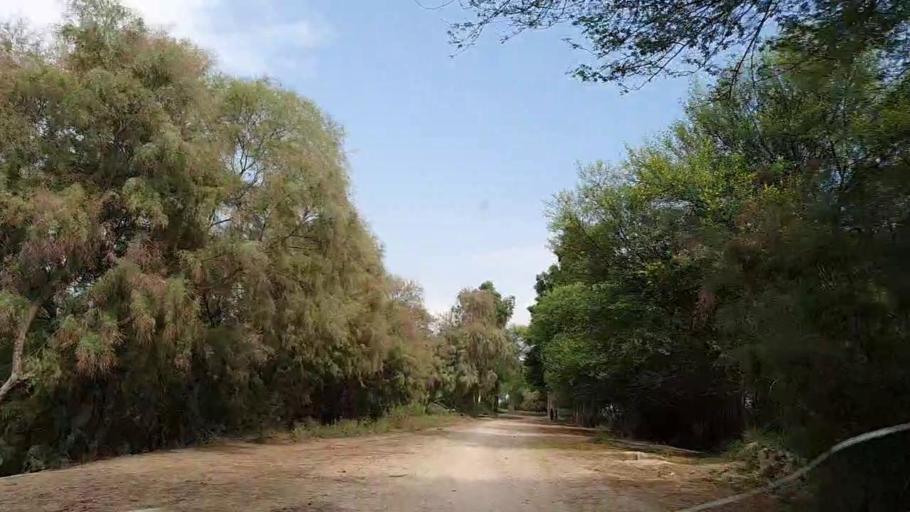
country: PK
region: Sindh
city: Khanpur
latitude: 27.8325
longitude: 69.5042
